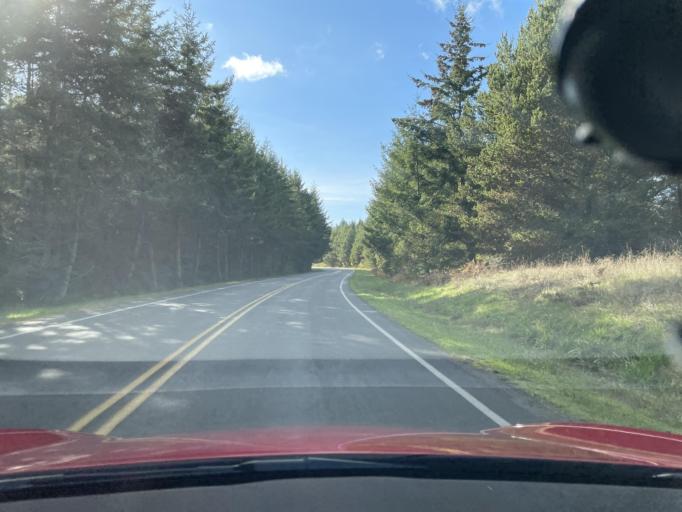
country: US
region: Washington
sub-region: San Juan County
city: Friday Harbor
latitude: 48.4679
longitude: -123.0236
